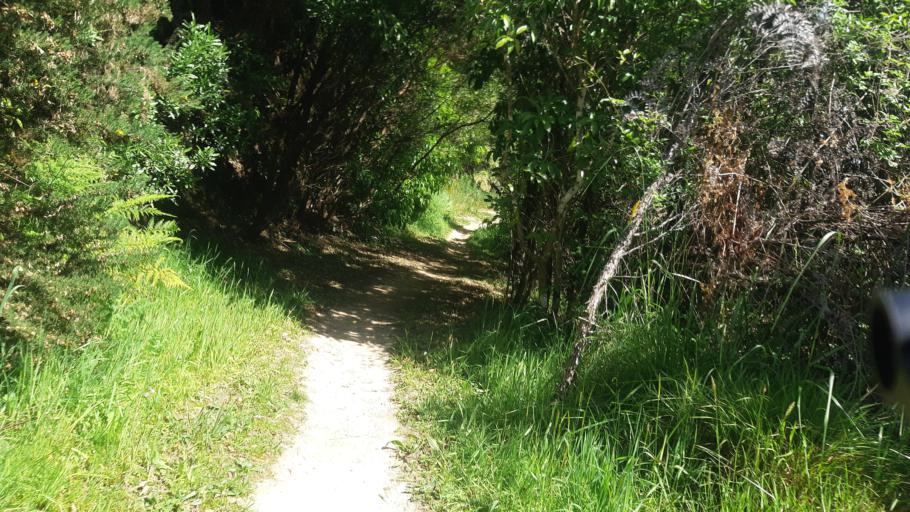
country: NZ
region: Marlborough
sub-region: Marlborough District
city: Picton
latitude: -41.2687
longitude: 174.0253
